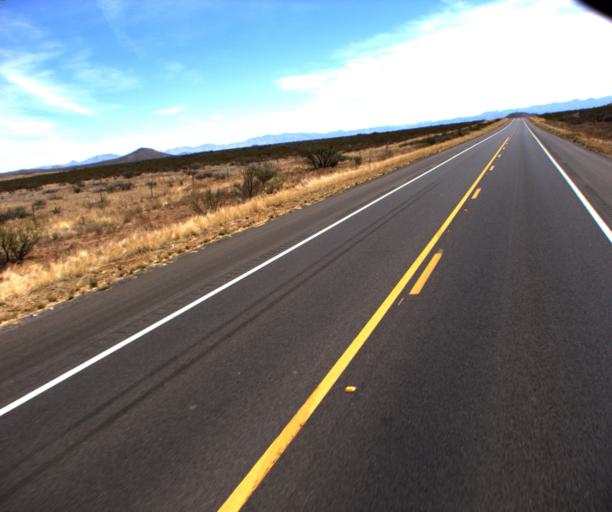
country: US
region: Arizona
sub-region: Cochise County
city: Willcox
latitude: 31.9055
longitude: -109.7597
